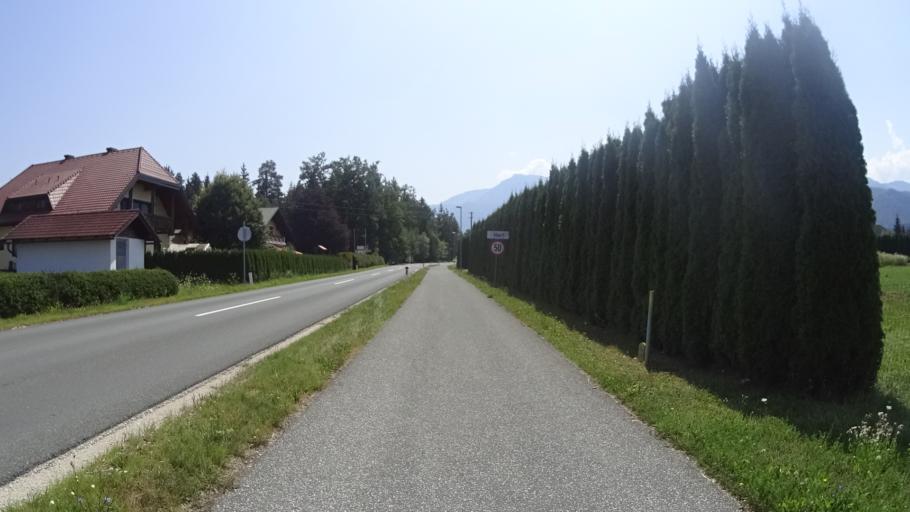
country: AT
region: Carinthia
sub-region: Politischer Bezirk Volkermarkt
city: Eberndorf
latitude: 46.5747
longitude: 14.6573
